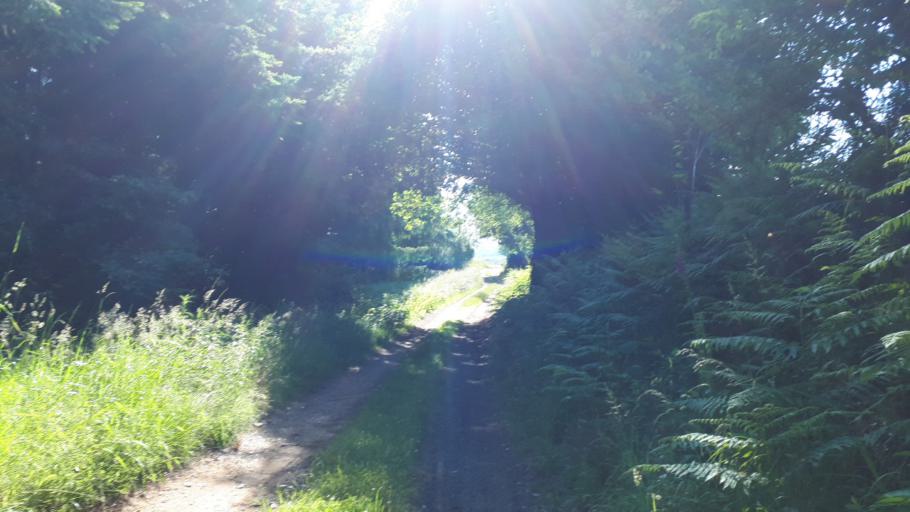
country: FR
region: Centre
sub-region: Departement du Loir-et-Cher
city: Sarge-sur-Braye
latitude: 47.9322
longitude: 0.8739
